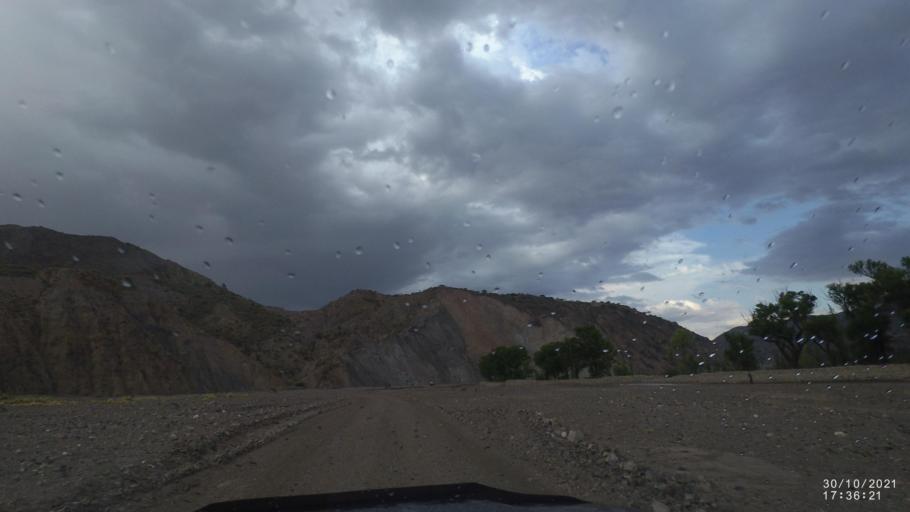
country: BO
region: Cochabamba
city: Sipe Sipe
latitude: -17.5251
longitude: -66.5666
